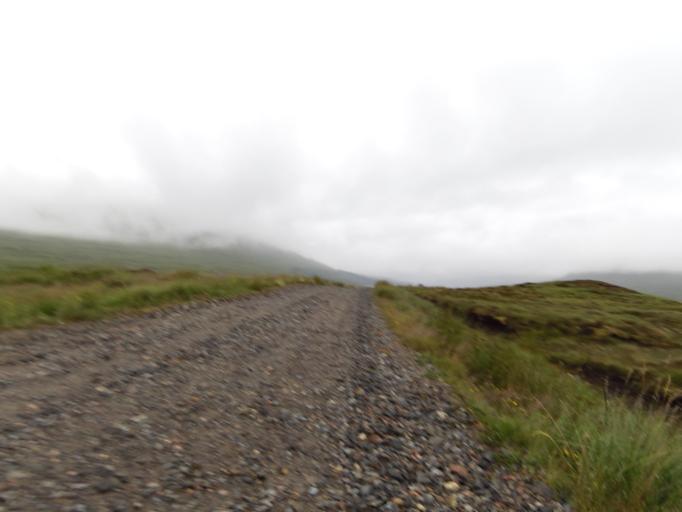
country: GB
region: Scotland
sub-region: Highland
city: Spean Bridge
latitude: 56.7621
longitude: -4.6845
